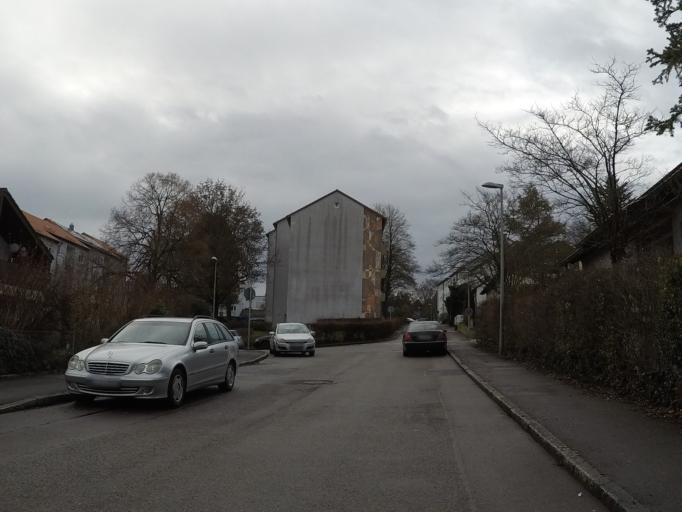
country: DE
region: Baden-Wuerttemberg
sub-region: Tuebingen Region
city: Ulm
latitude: 48.3887
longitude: 9.9559
